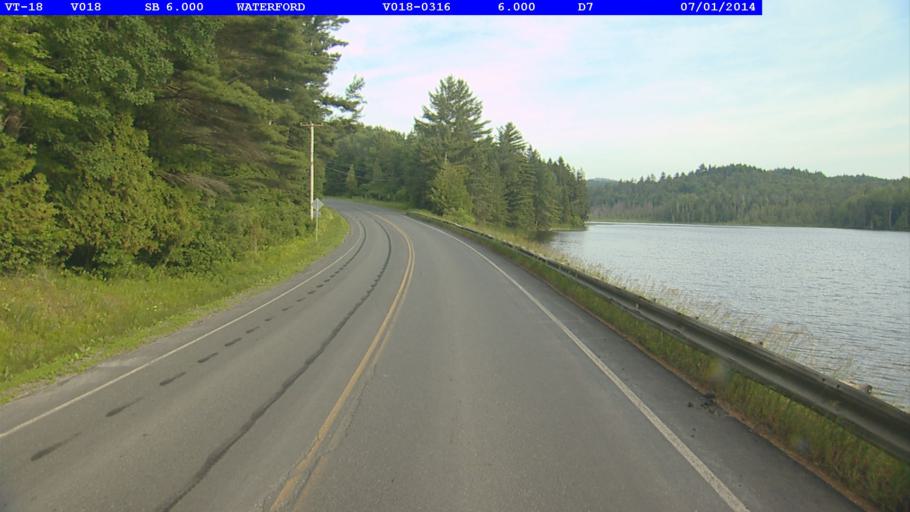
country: US
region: Vermont
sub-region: Caledonia County
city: Saint Johnsbury
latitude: 44.4145
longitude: -71.9366
